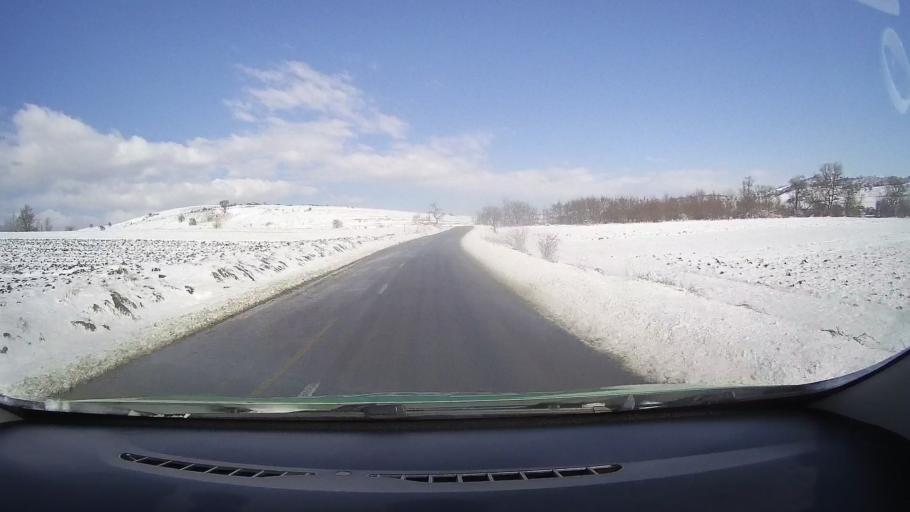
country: RO
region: Sibiu
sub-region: Comuna Vurpar
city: Vurpar
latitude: 45.8766
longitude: 24.3207
